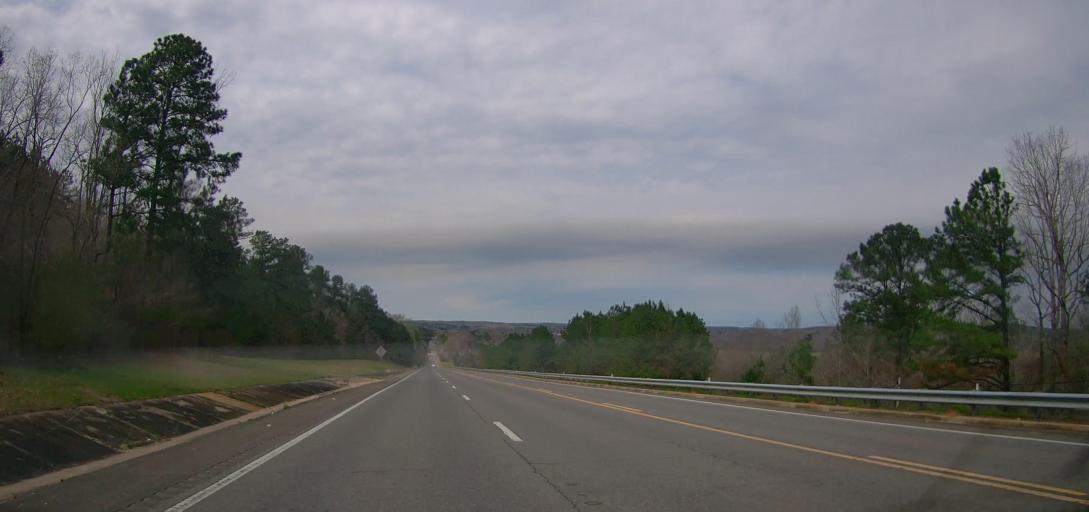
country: US
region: Alabama
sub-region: Marion County
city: Hamilton
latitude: 34.0848
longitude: -87.9789
